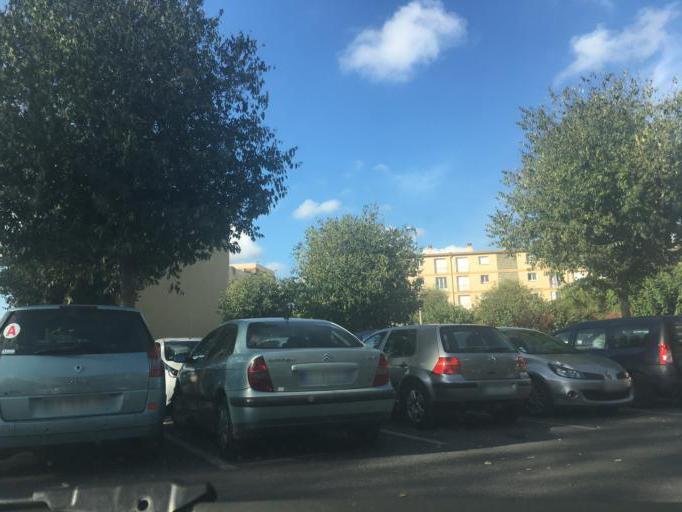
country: FR
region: Provence-Alpes-Cote d'Azur
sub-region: Departement du Var
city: Draguignan
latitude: 43.5393
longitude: 6.4596
